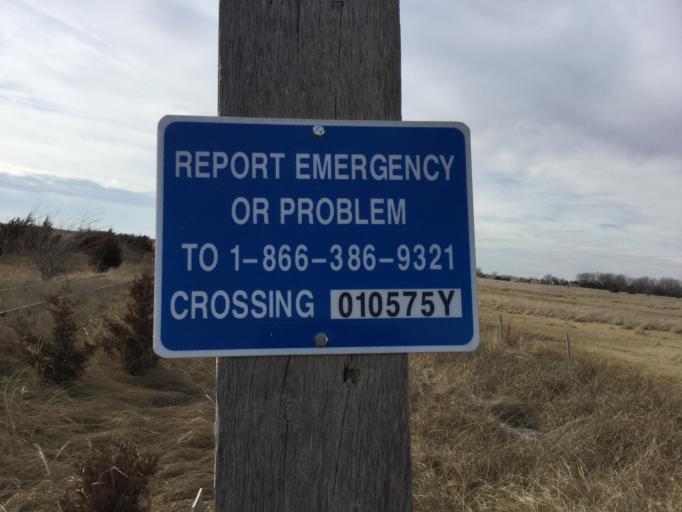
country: US
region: Kansas
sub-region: Rice County
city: Lyons
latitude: 38.3517
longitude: -98.3127
